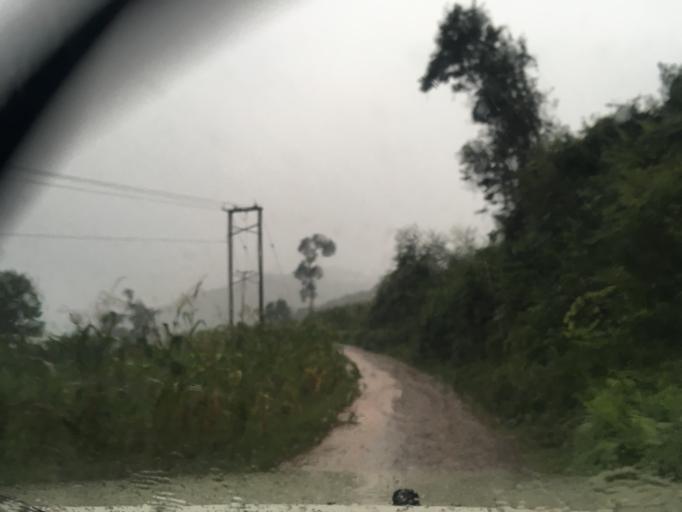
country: LA
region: Oudomxai
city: Muang La
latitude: 21.2377
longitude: 101.9564
